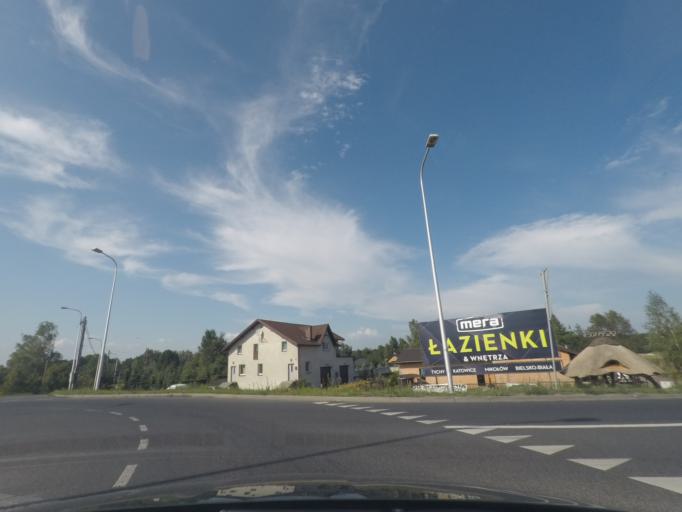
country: PL
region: Silesian Voivodeship
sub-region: Zory
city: Zory
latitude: 50.0586
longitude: 18.6828
